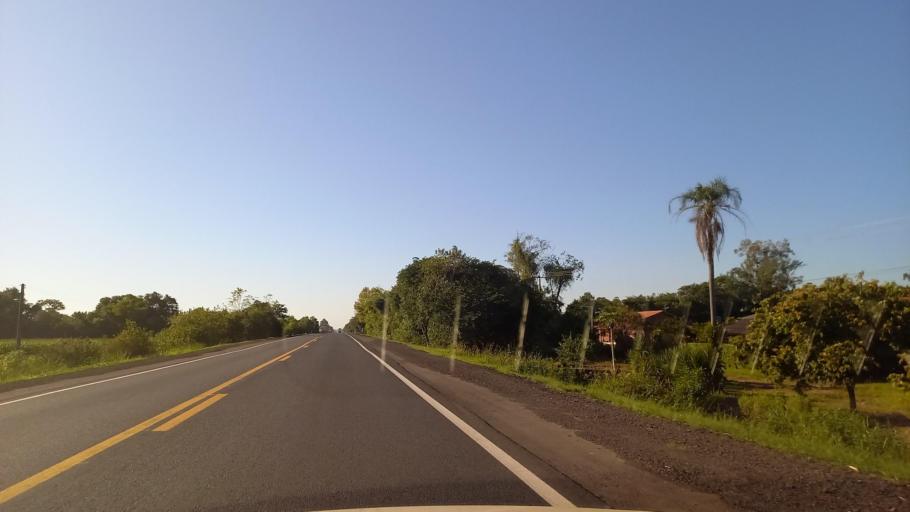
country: BR
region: Rio Grande do Sul
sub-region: Venancio Aires
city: Venancio Aires
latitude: -29.6589
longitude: -52.0774
